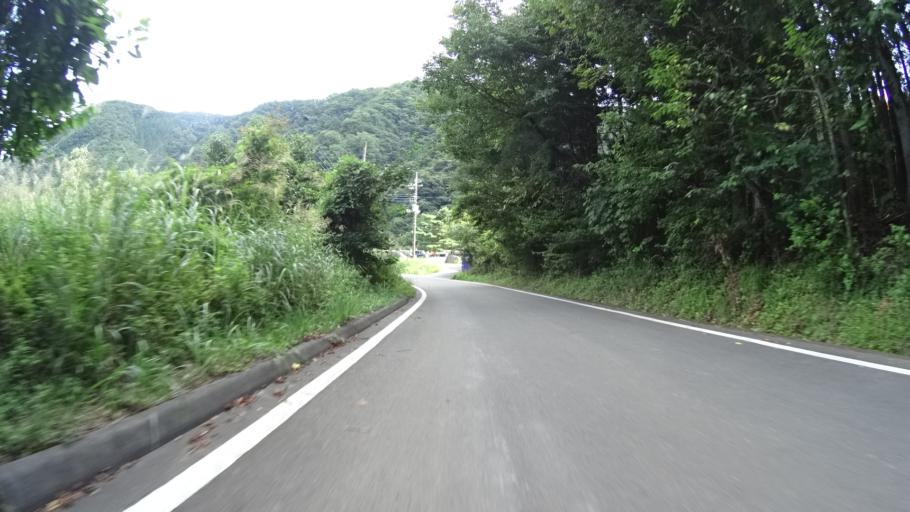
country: JP
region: Yamanashi
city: Enzan
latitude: 35.5999
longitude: 138.7989
